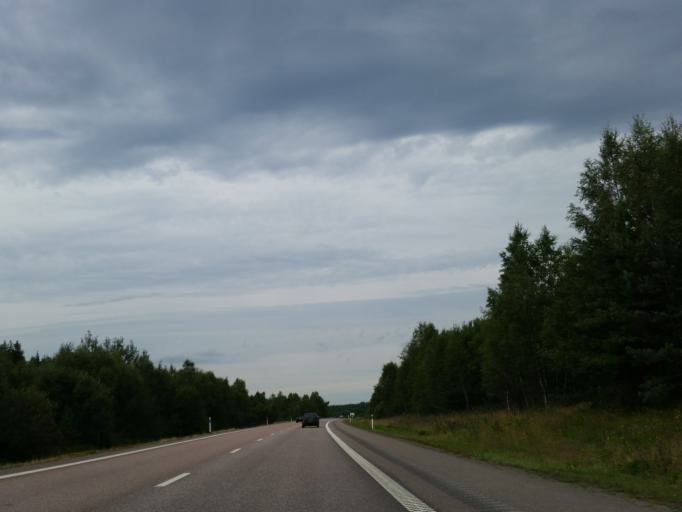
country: SE
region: Soedermanland
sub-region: Strangnas Kommun
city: Mariefred
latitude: 59.2294
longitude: 17.2085
